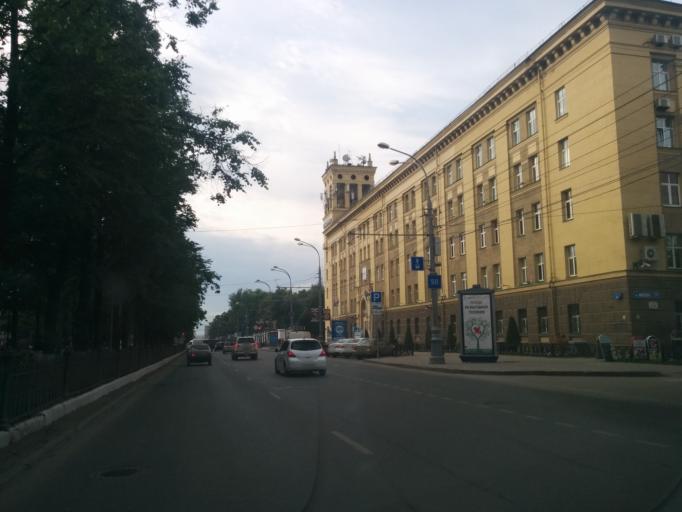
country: RU
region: Perm
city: Perm
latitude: 58.0014
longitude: 56.2485
